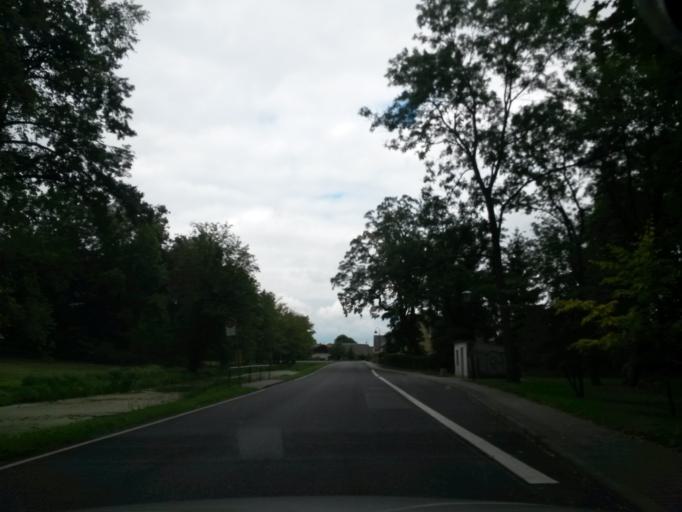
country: DE
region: Brandenburg
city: Gerswalde
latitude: 53.1576
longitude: 13.8479
